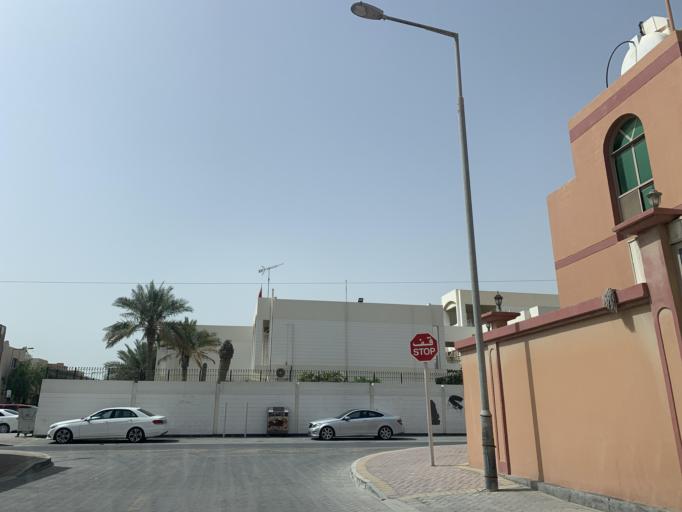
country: BH
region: Northern
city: Sitrah
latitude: 26.1369
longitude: 50.6006
